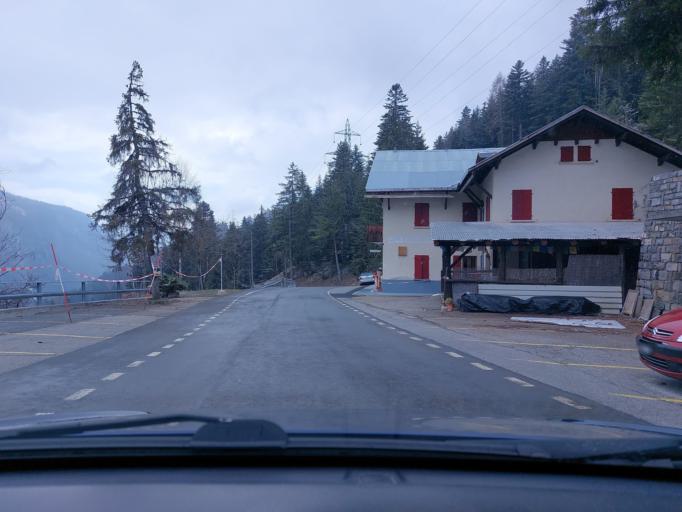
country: CH
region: Valais
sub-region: Sion District
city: Saviese
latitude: 46.2935
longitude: 7.3241
